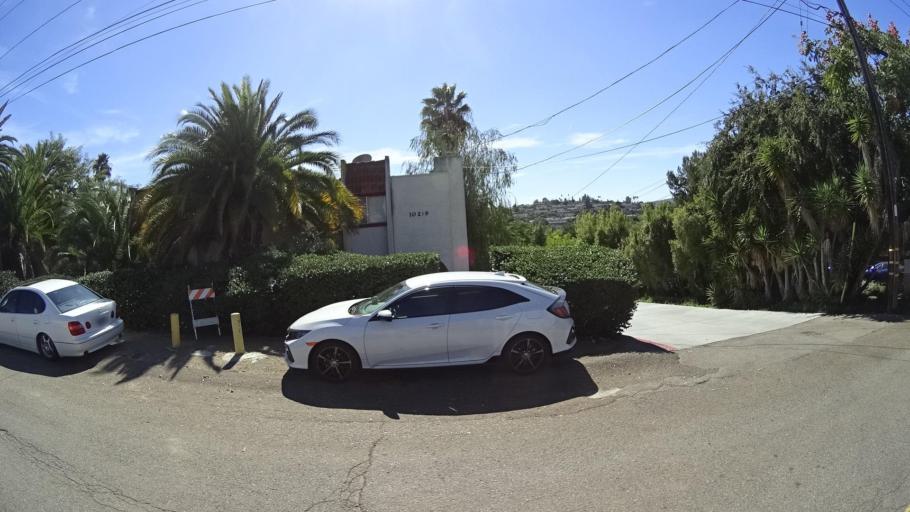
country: US
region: California
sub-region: San Diego County
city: Casa de Oro-Mount Helix
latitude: 32.7461
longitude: -116.9739
